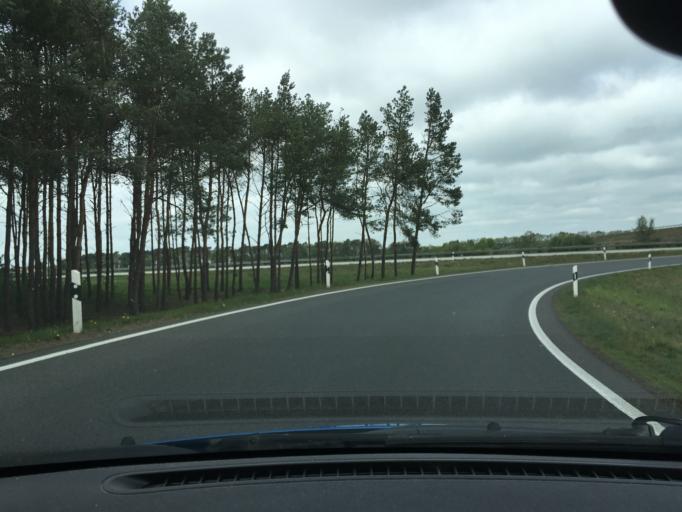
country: DE
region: Mecklenburg-Vorpommern
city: Rastow
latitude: 53.4300
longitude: 11.4909
